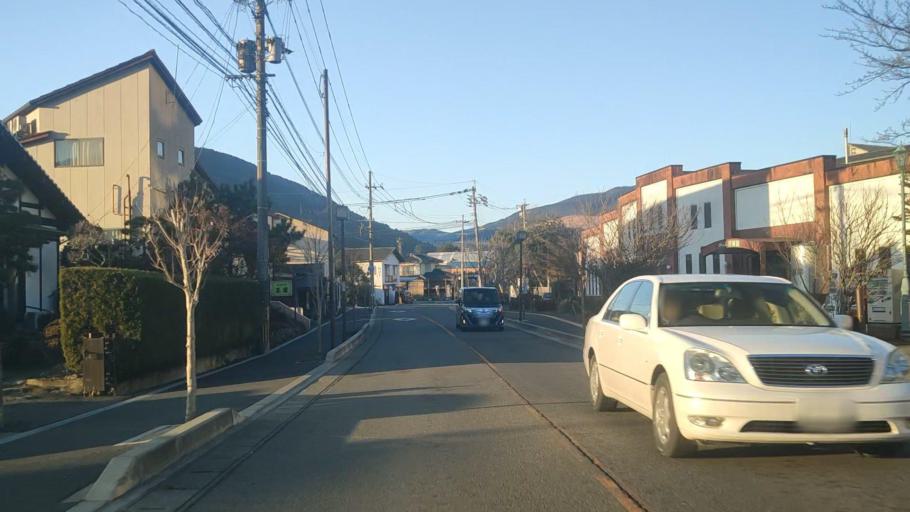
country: JP
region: Oita
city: Beppu
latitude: 33.2592
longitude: 131.3565
